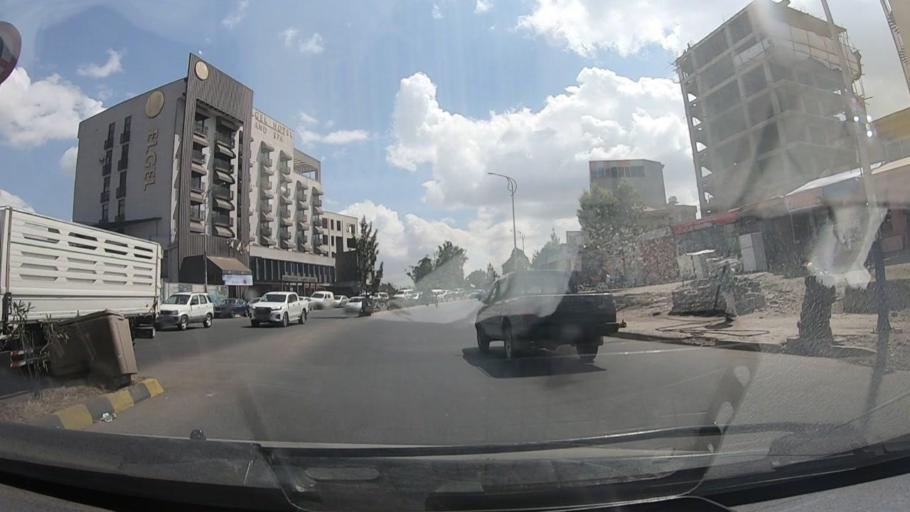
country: ET
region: Adis Abeba
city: Addis Ababa
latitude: 8.9802
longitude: 38.7217
